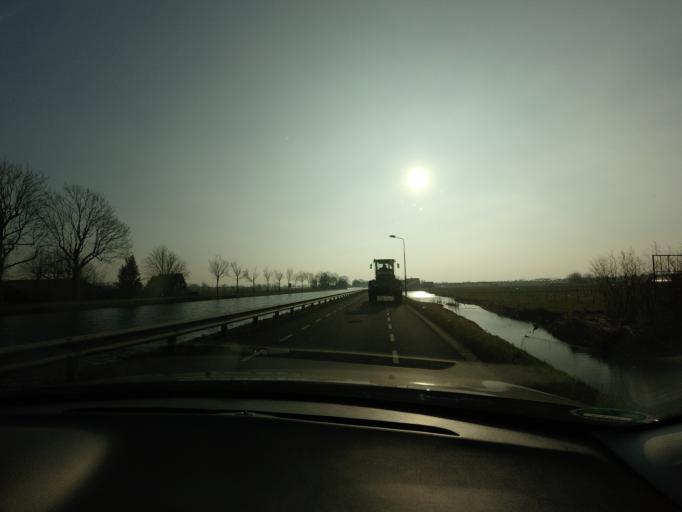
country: NL
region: South Holland
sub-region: Gemeente Nieuwkoop
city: Nieuwkoop
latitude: 52.1910
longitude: 4.7359
